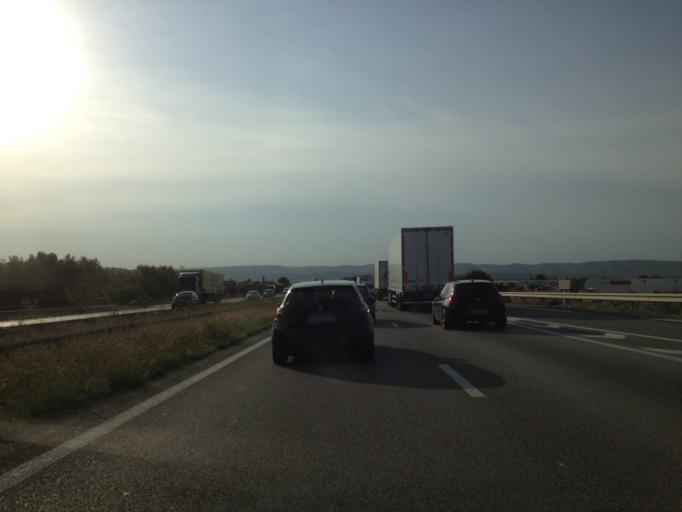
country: FR
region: Provence-Alpes-Cote d'Azur
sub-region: Departement des Bouches-du-Rhone
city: Vitrolles
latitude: 43.4453
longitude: 5.2432
